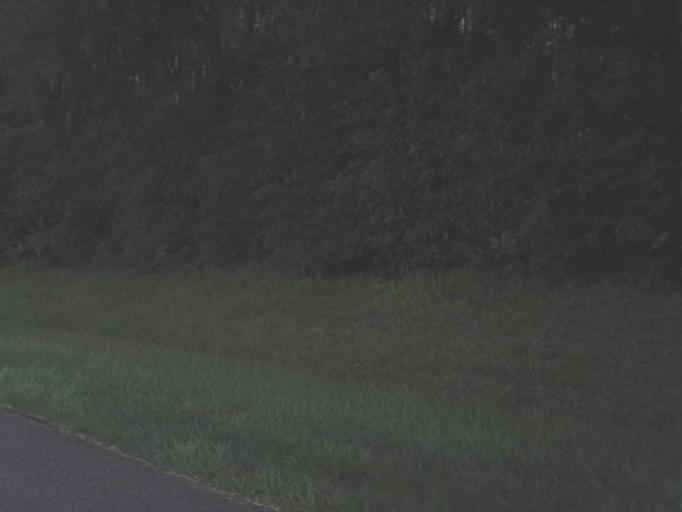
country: US
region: Florida
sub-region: Gilchrist County
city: Trenton
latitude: 29.6602
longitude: -82.8459
